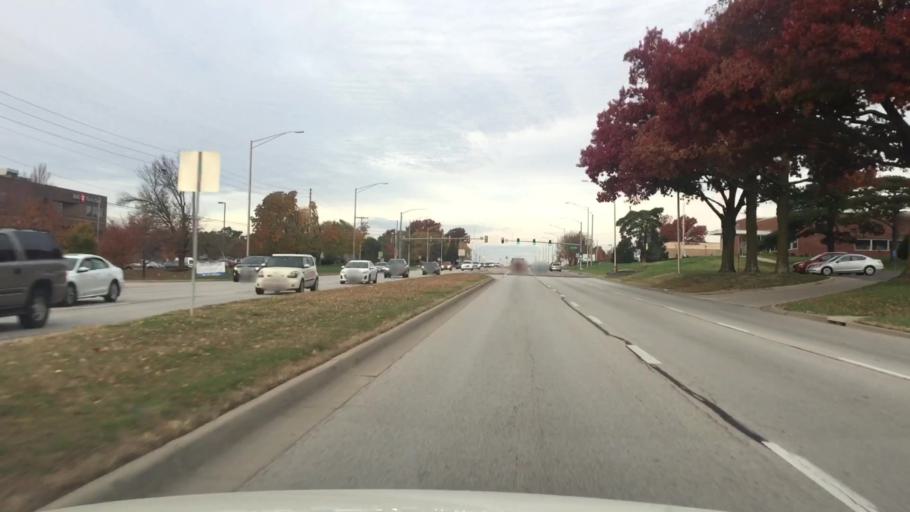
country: US
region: Kansas
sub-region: Johnson County
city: Shawnee
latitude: 39.0148
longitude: -94.7286
